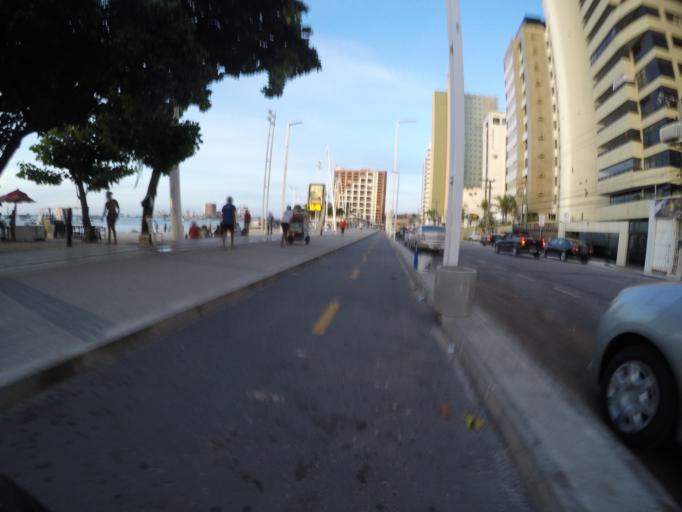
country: BR
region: Ceara
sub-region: Fortaleza
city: Fortaleza
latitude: -3.7224
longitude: -38.4815
